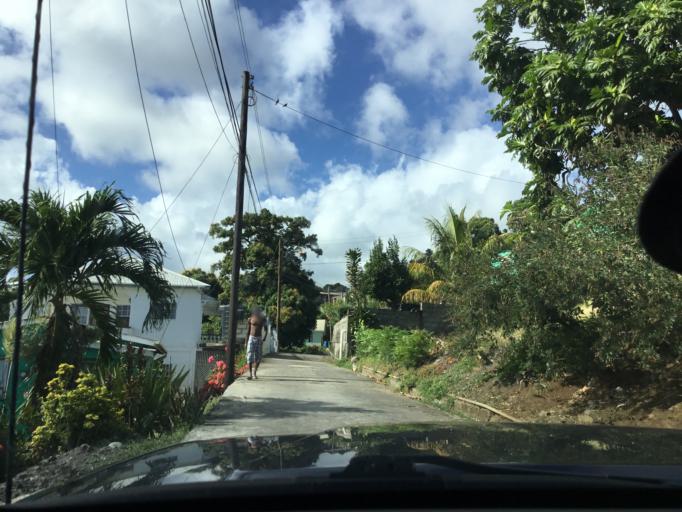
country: VC
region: Charlotte
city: Biabou
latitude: 13.1483
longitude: -61.1568
